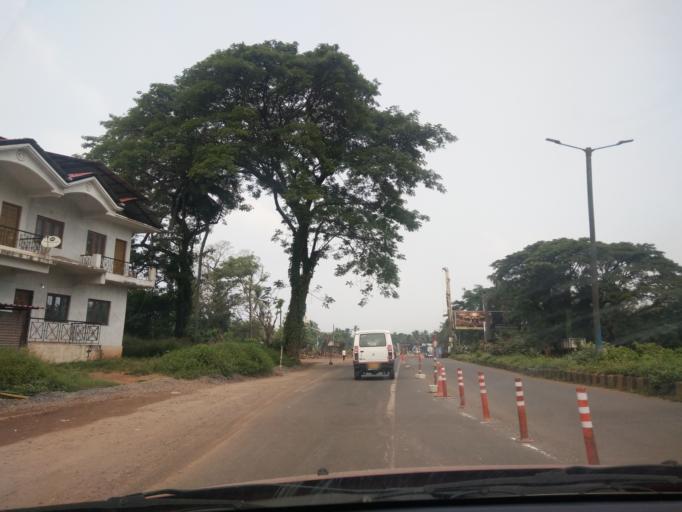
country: IN
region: Goa
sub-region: South Goa
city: Cortalim
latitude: 15.4209
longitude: 73.9016
